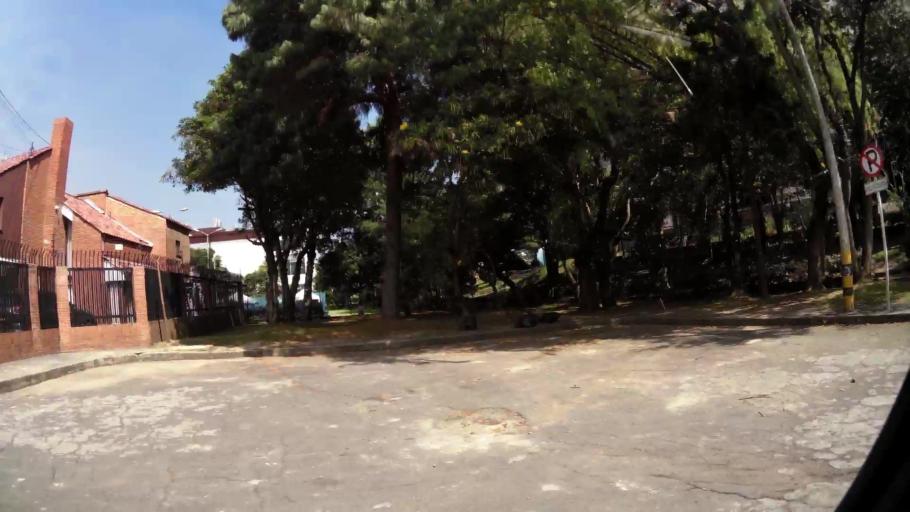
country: CO
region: Bogota D.C.
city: Barrio San Luis
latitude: 4.6910
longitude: -74.0353
